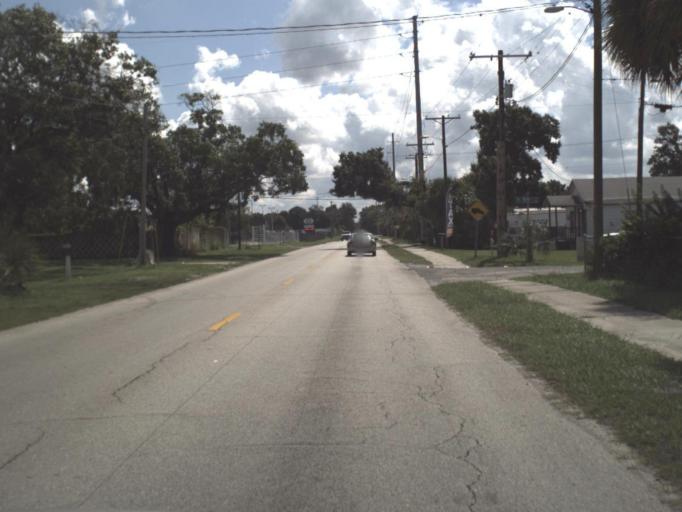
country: US
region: Florida
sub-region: Hillsborough County
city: East Lake-Orient Park
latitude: 27.9668
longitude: -82.3947
